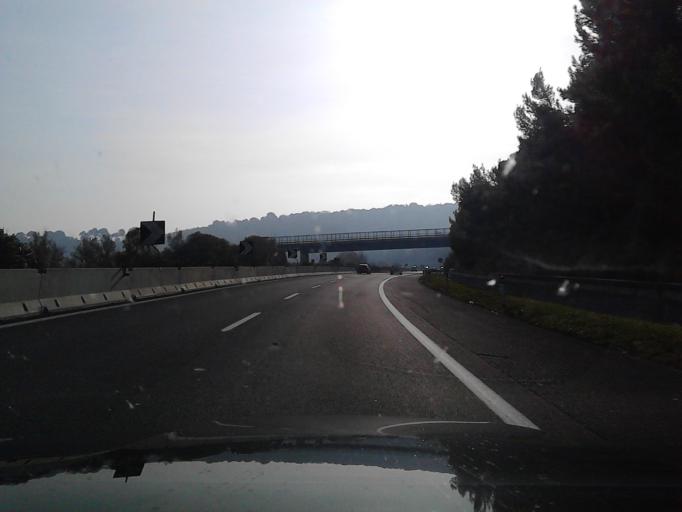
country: IT
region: The Marches
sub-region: Province of Fermo
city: Campofilone
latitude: 43.0606
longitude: 13.8466
